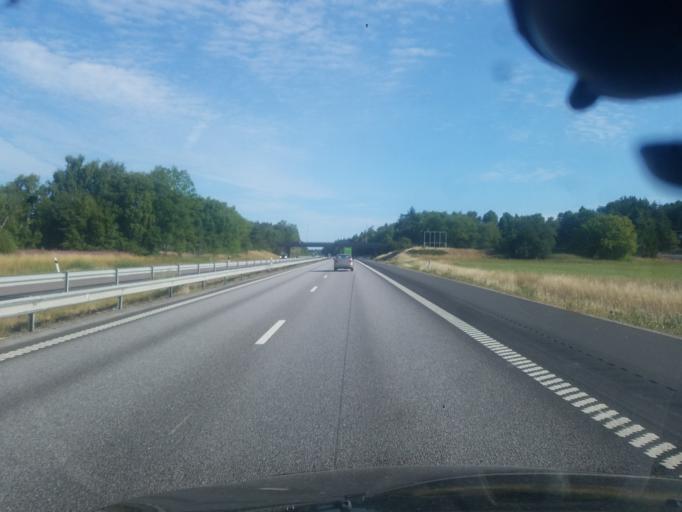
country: SE
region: Vaestra Goetaland
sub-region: Stenungsunds Kommun
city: Stora Hoga
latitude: 57.9834
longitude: 11.8418
